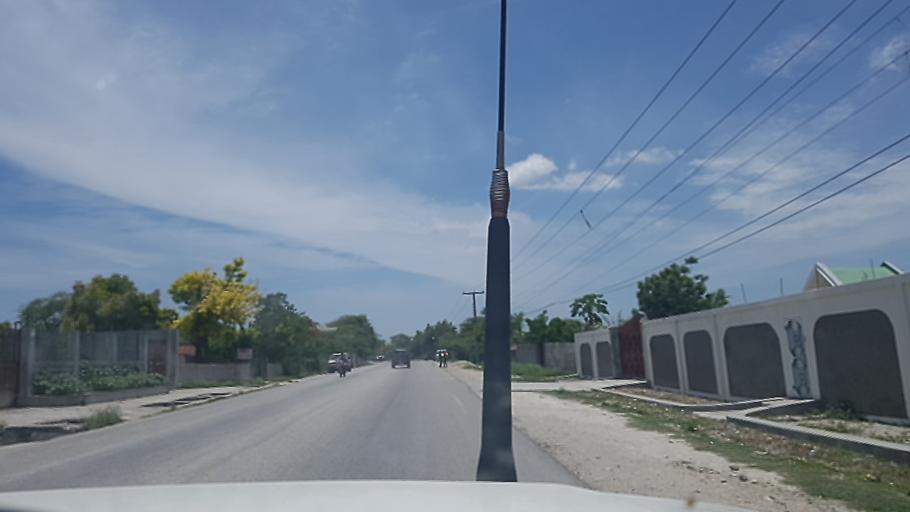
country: HT
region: Artibonite
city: Saint-Marc
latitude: 19.1513
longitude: -72.6241
